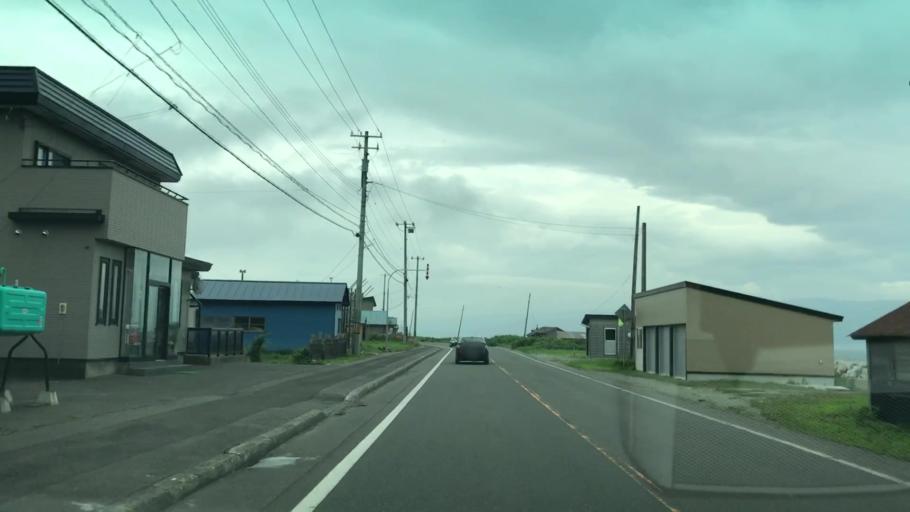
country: JP
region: Hokkaido
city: Iwanai
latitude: 42.8264
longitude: 140.3060
